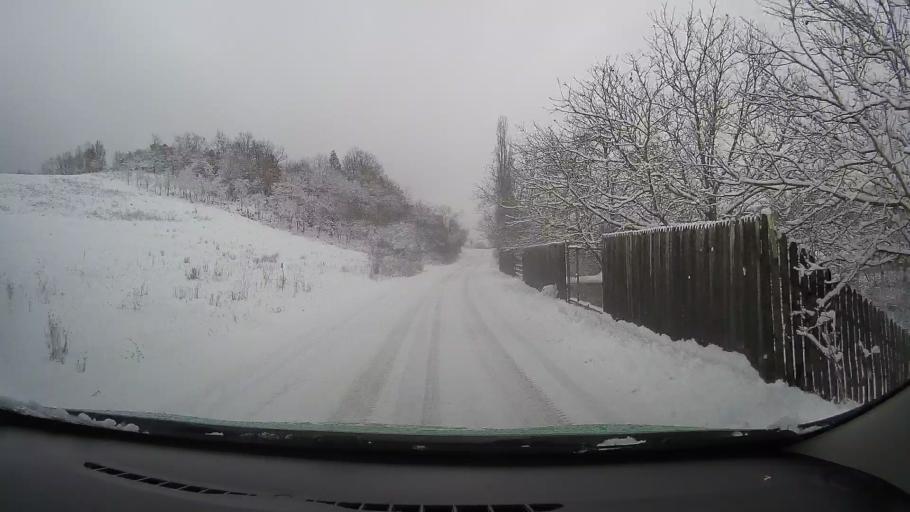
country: RO
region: Hunedoara
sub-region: Comuna Pestisu Mic
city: Pestisu Mic
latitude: 45.8242
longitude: 22.8607
